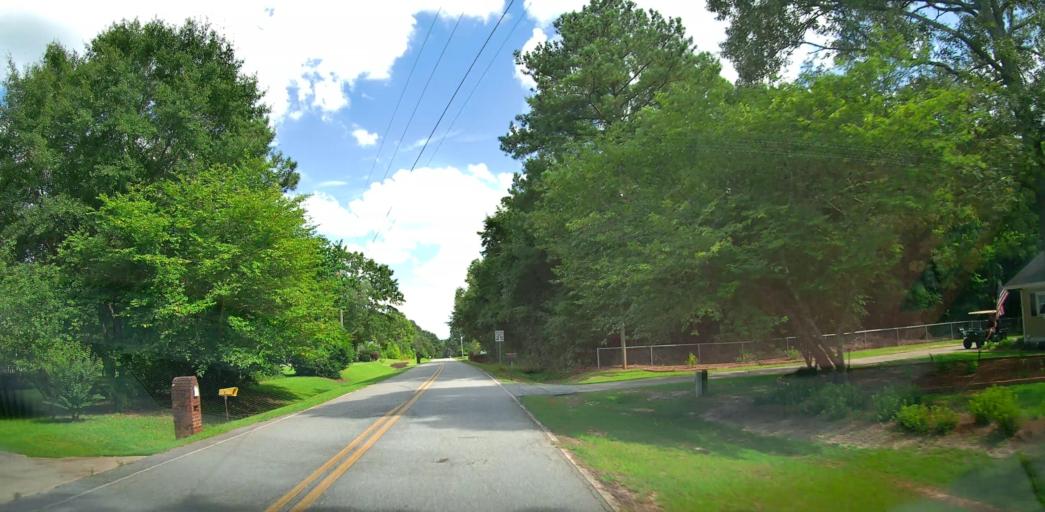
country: US
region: Georgia
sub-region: Houston County
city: Centerville
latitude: 32.5831
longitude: -83.6680
